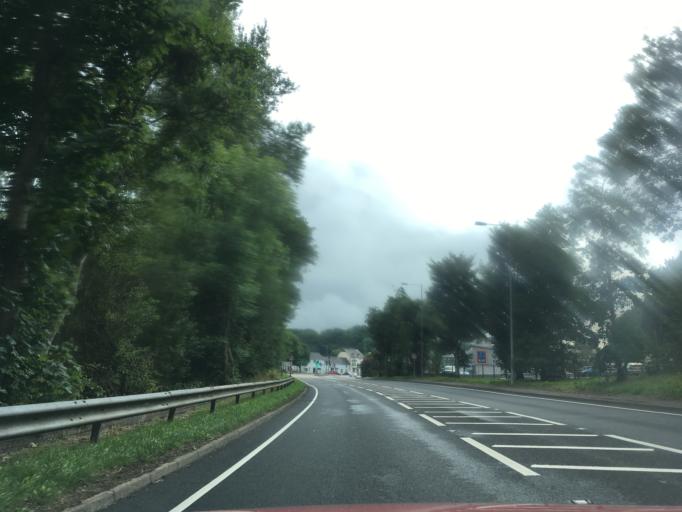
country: GB
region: Wales
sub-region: Pembrokeshire
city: Haverfordwest
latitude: 51.8037
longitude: -4.9609
